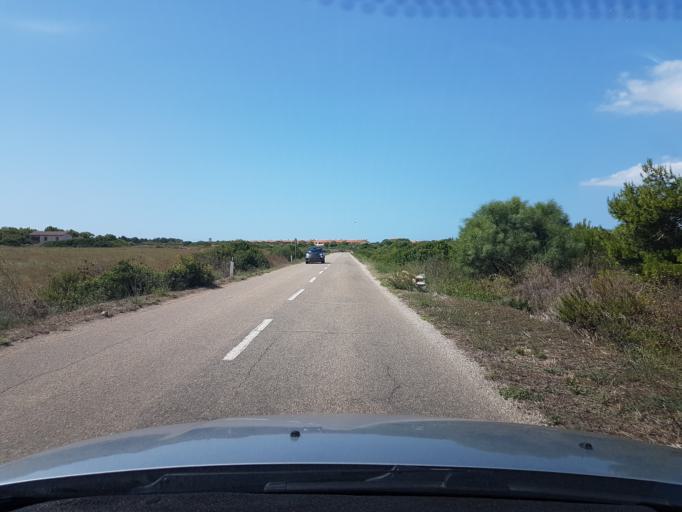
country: IT
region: Sardinia
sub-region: Provincia di Oristano
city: Riola Sardo
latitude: 40.0366
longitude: 8.4201
